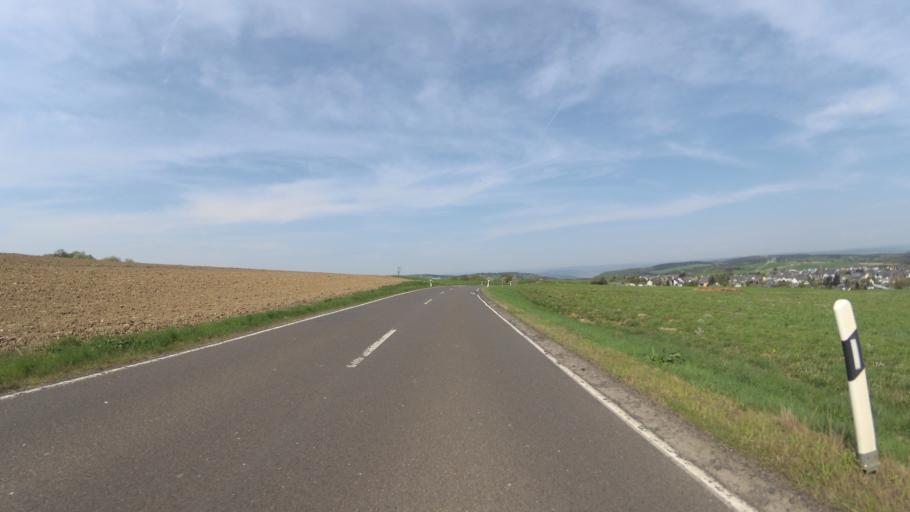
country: DE
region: Rheinland-Pfalz
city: Longkamp
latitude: 49.8827
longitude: 7.1205
